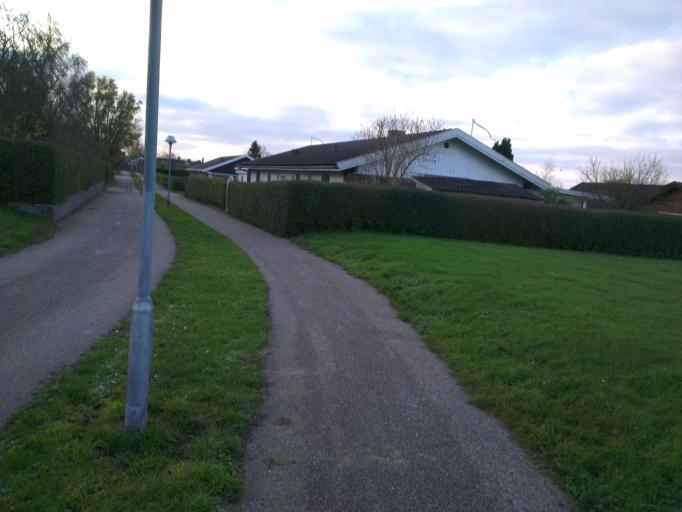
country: DK
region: Capital Region
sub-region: Frederikssund Kommune
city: Jaegerspris
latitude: 55.8503
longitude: 11.9965
